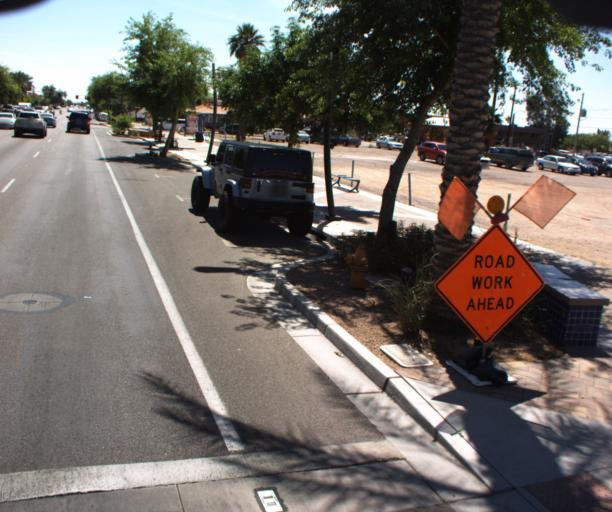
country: US
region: Arizona
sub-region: Maricopa County
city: Chandler
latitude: 33.3013
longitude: -111.8415
